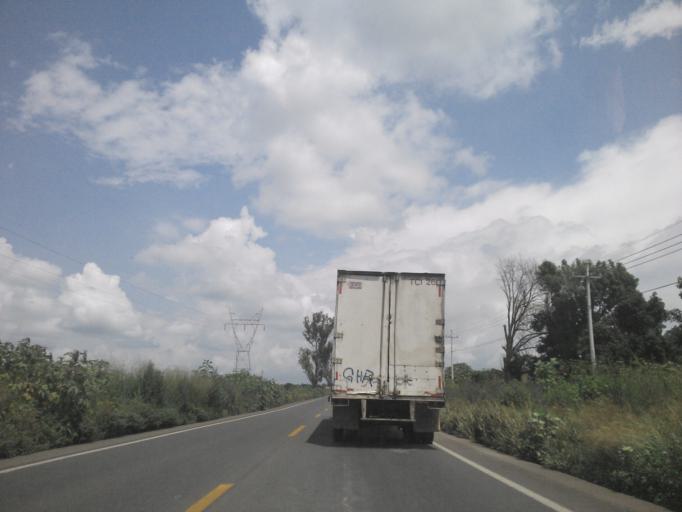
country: MX
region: Jalisco
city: Acatic
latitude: 20.7126
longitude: -102.9418
